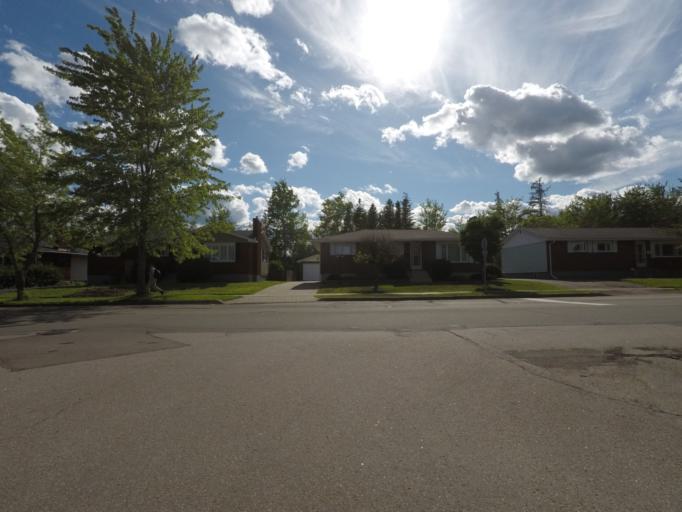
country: CA
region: New Brunswick
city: Moncton
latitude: 46.0970
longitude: -64.8269
